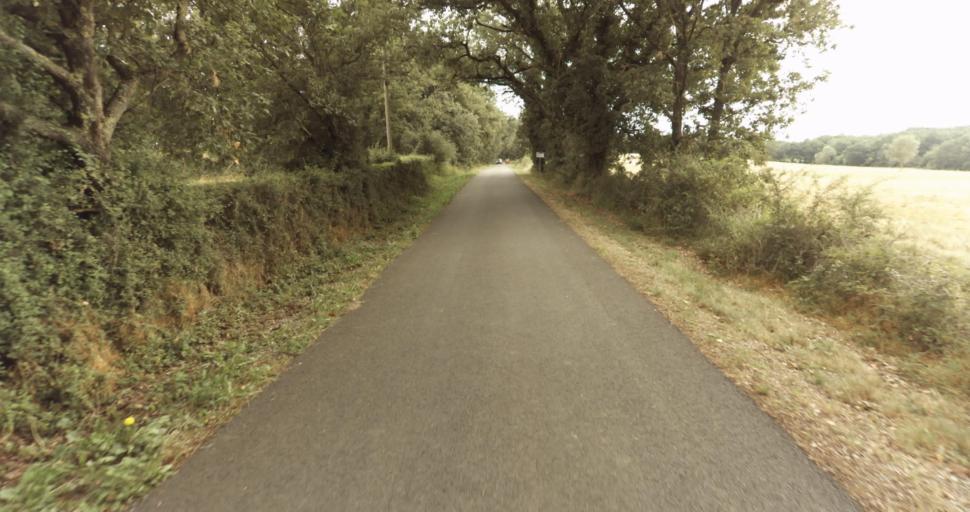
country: FR
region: Midi-Pyrenees
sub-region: Departement de la Haute-Garonne
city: Fonsorbes
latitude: 43.5577
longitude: 1.2421
